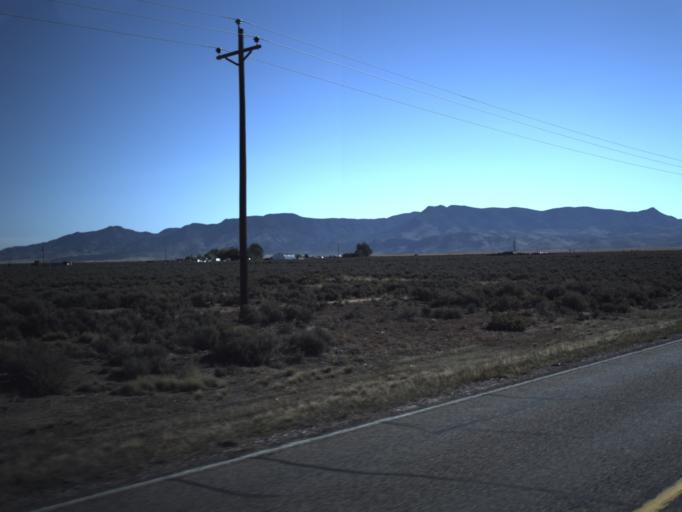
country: US
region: Utah
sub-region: Washington County
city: Enterprise
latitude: 37.6926
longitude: -113.6093
